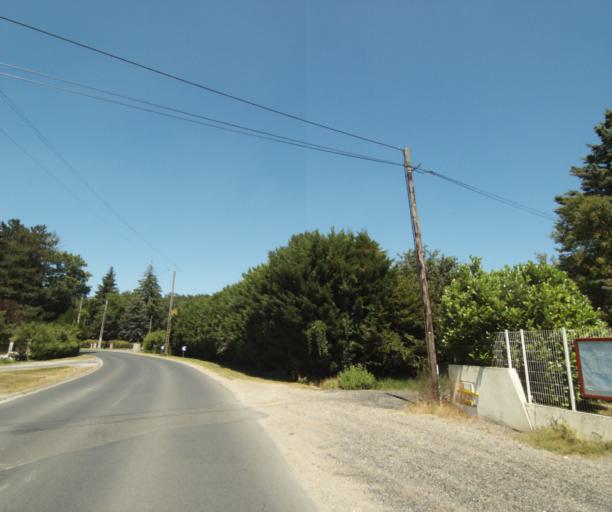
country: FR
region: Ile-de-France
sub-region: Departement de Seine-et-Marne
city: Noisy-sur-Ecole
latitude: 48.3619
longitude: 2.5204
